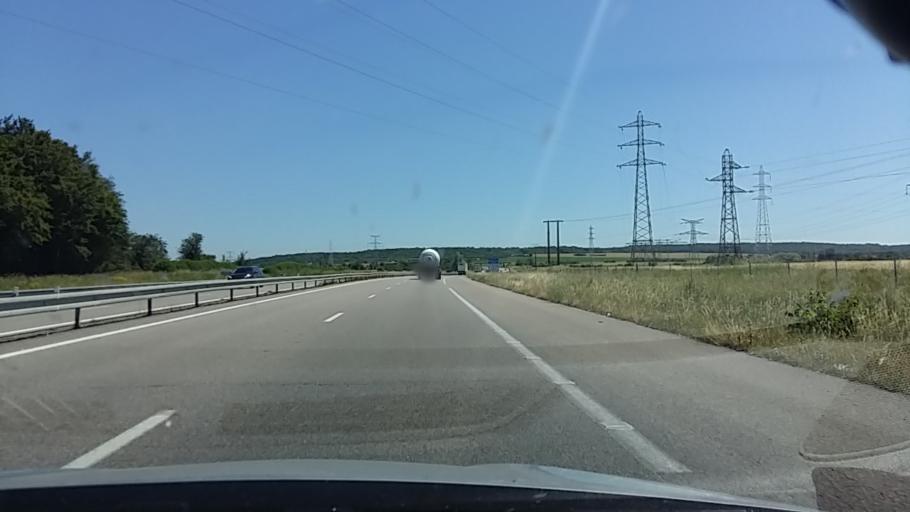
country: FR
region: Lorraine
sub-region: Departement de la Moselle
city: Saint-Privat-la-Montagne
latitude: 49.1814
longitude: 6.0305
